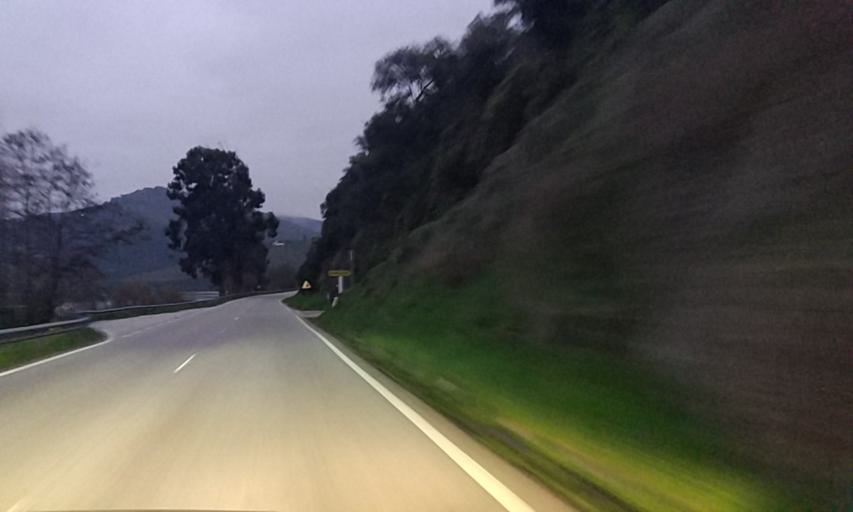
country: PT
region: Viseu
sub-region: Tabuaco
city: Tabuaco
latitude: 41.1578
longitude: -7.6122
